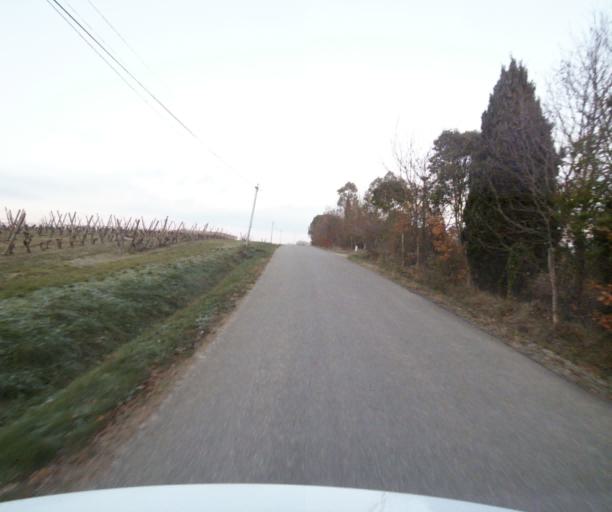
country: FR
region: Midi-Pyrenees
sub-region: Departement du Tarn-et-Garonne
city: Moissac
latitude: 44.1221
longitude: 1.0562
